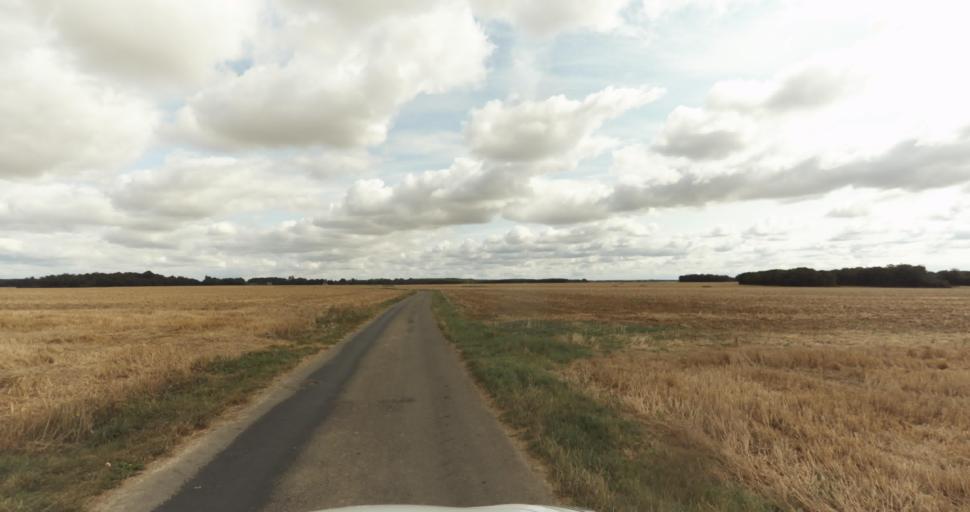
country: FR
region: Haute-Normandie
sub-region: Departement de l'Eure
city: Nonancourt
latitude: 48.7875
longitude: 1.1518
